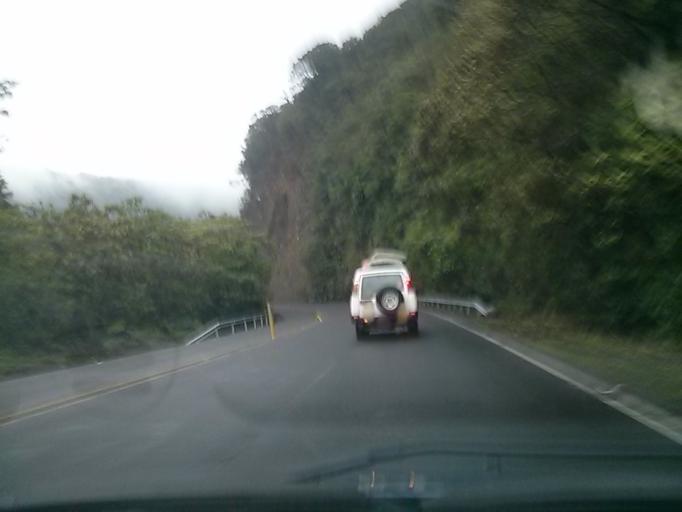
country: CR
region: Heredia
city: Angeles
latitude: 10.0586
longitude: -84.0089
